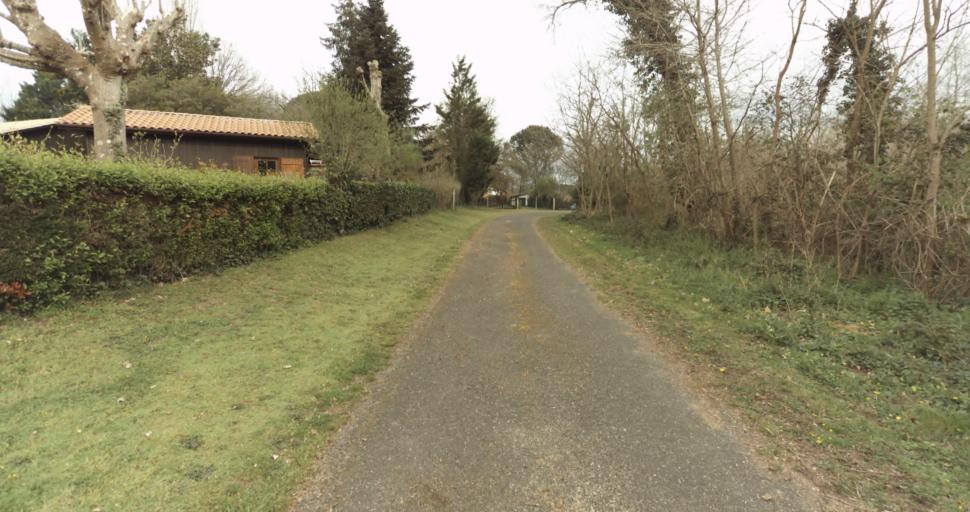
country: FR
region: Aquitaine
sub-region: Departement des Landes
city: Roquefort
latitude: 44.0404
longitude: -0.3177
